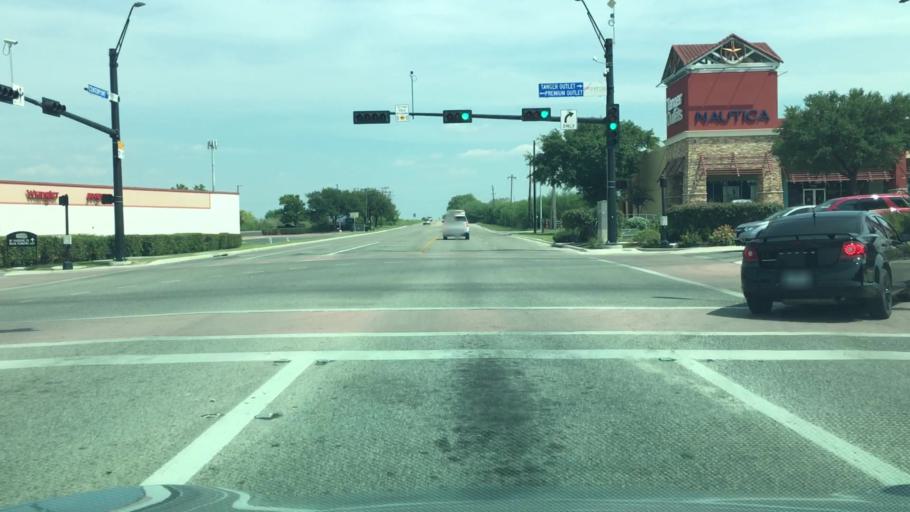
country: US
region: Texas
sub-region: Hays County
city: San Marcos
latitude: 29.8265
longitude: -97.9840
